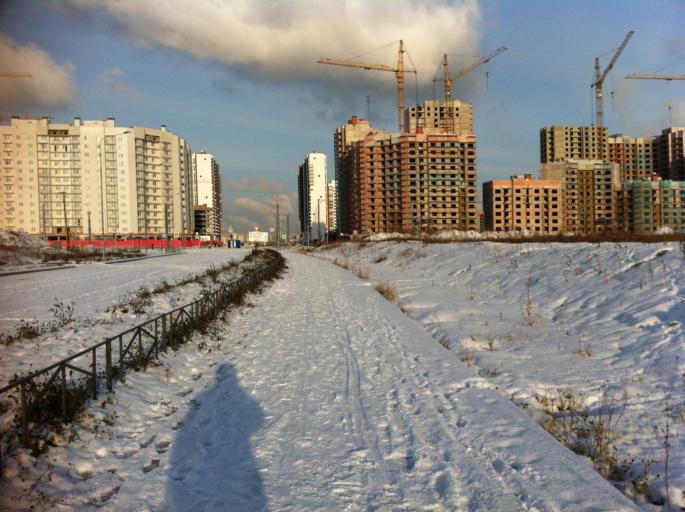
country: RU
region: St.-Petersburg
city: Sosnovaya Polyana
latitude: 59.8652
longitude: 30.1557
